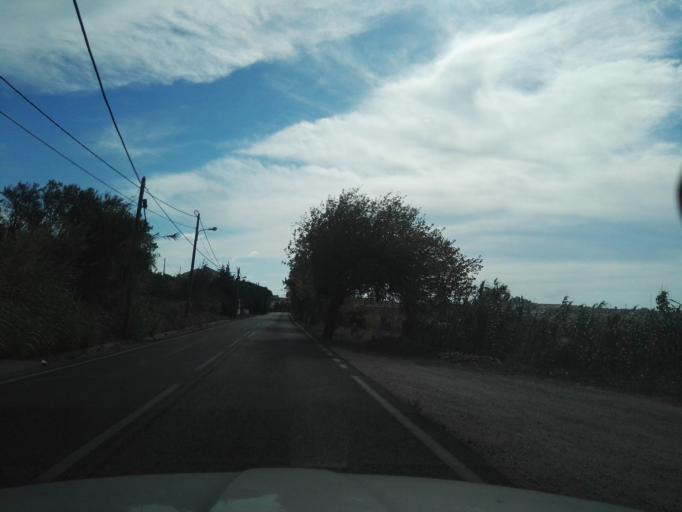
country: PT
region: Lisbon
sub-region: Vila Franca de Xira
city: Sao Joao dos Montes
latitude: 38.9604
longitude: -9.0311
